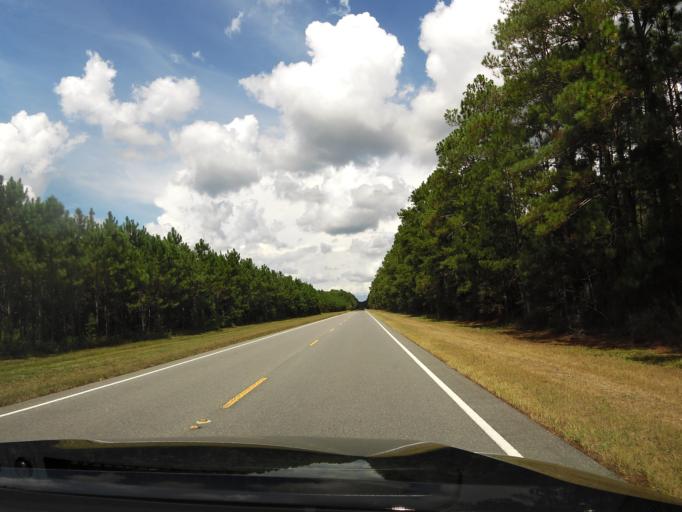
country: US
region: Georgia
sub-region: Charlton County
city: Folkston
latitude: 30.9943
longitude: -82.0263
